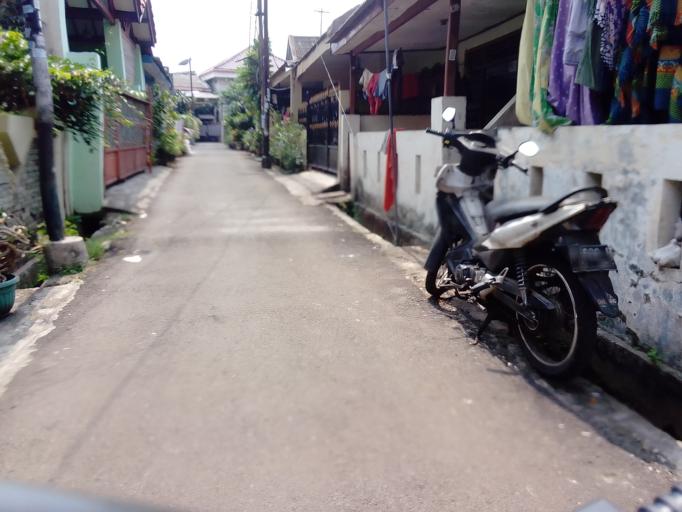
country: ID
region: Jakarta Raya
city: Jakarta
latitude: -6.2166
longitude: 106.8116
